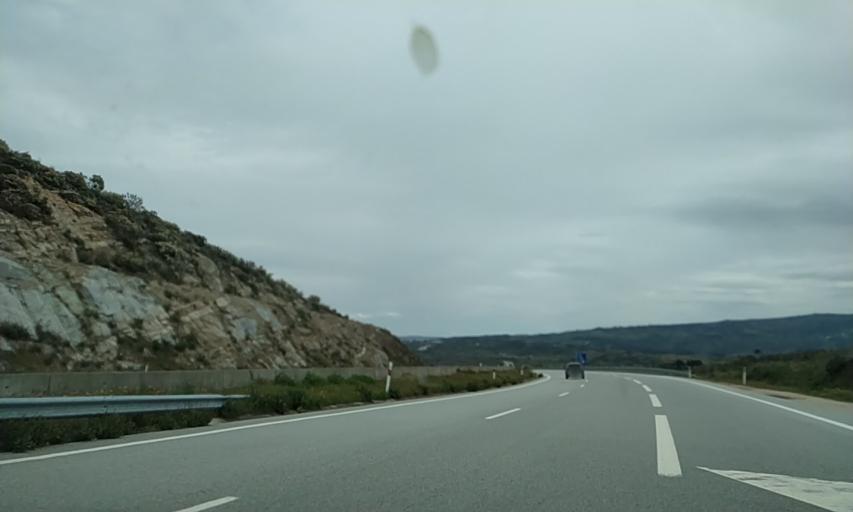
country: PT
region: Guarda
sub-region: Celorico da Beira
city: Celorico da Beira
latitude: 40.6351
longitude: -7.4528
